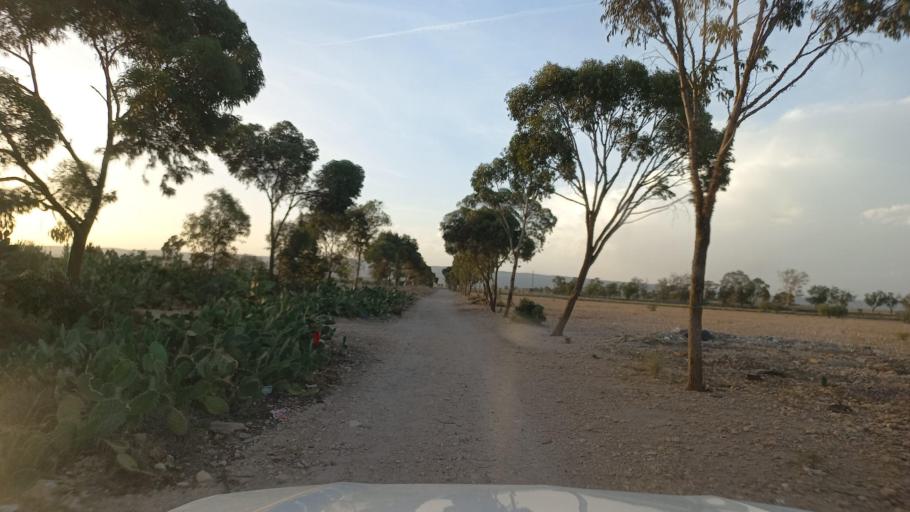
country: TN
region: Al Qasrayn
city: Kasserine
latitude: 35.2403
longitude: 8.9939
